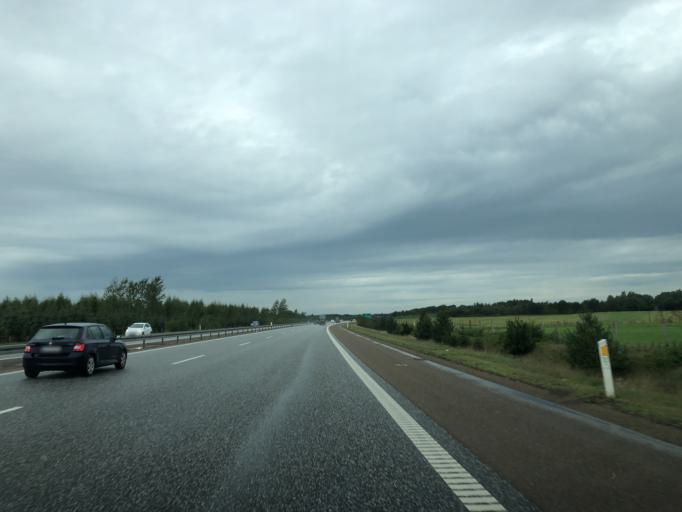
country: DK
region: Central Jutland
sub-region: Herning Kommune
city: Lind
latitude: 56.0178
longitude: 9.0185
